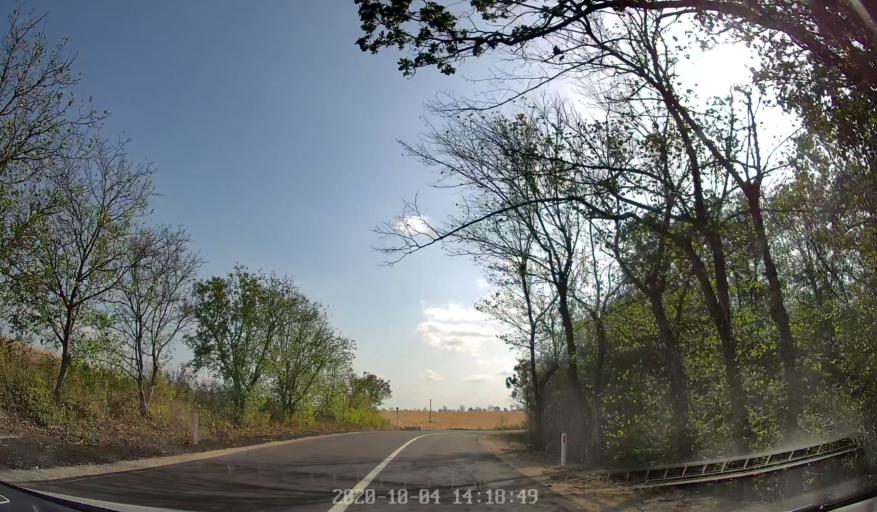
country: MD
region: Rezina
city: Saharna
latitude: 47.5963
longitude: 28.9768
